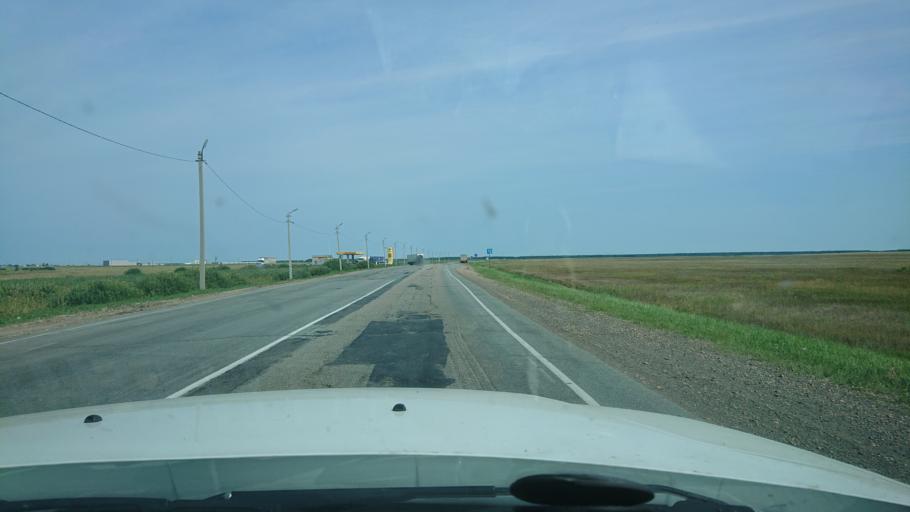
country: RU
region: Tjumen
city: Armizonskoye
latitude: 55.5346
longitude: 67.8913
